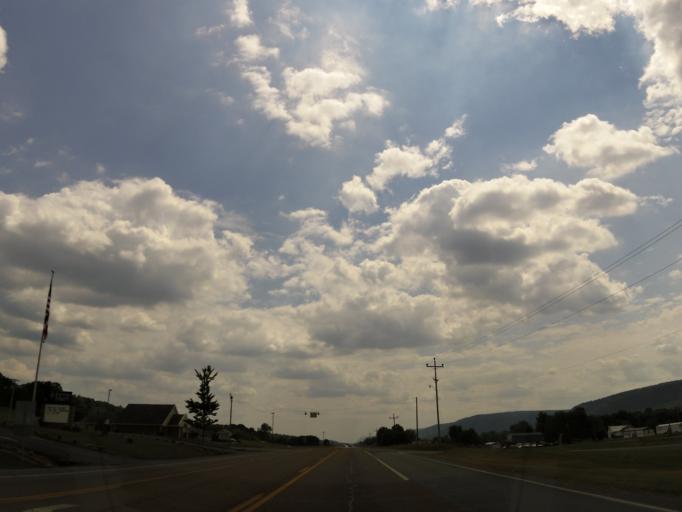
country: US
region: Tennessee
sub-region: Sequatchie County
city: Dunlap
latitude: 35.3547
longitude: -85.4009
